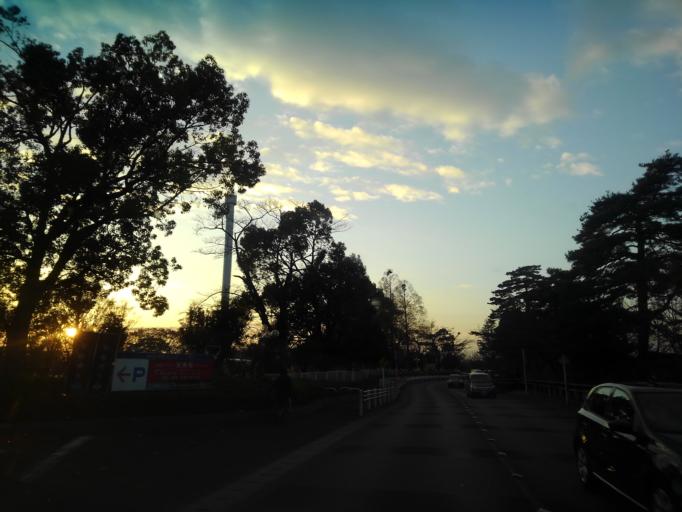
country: JP
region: Tokyo
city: Higashimurayama-shi
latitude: 35.7689
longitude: 139.4396
